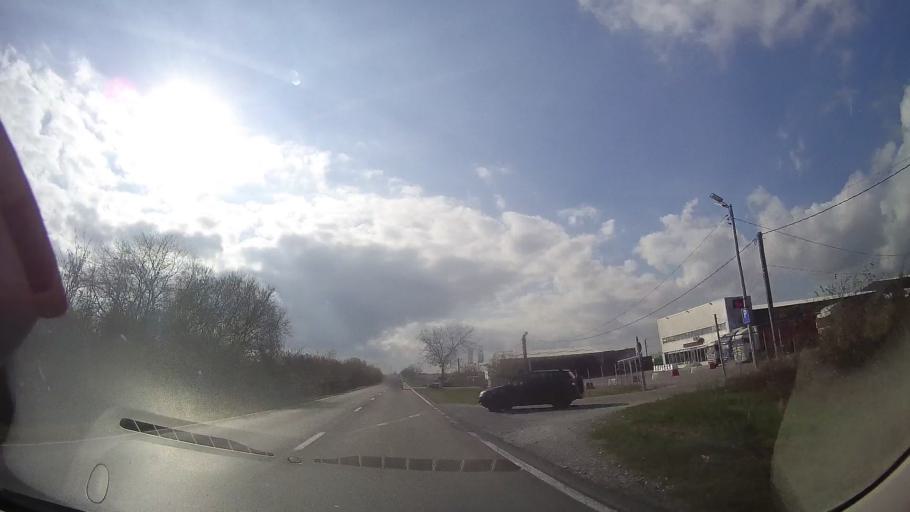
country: RO
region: Constanta
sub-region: Comuna Agigea
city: Agigea
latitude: 44.0825
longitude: 28.6052
